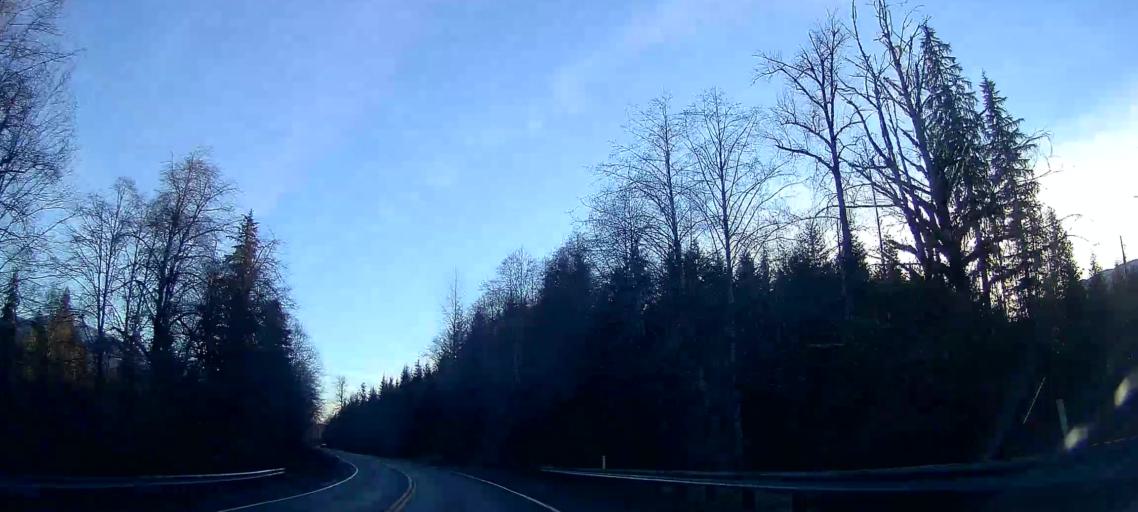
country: US
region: Washington
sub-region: Snohomish County
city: Darrington
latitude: 48.6333
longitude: -121.7406
